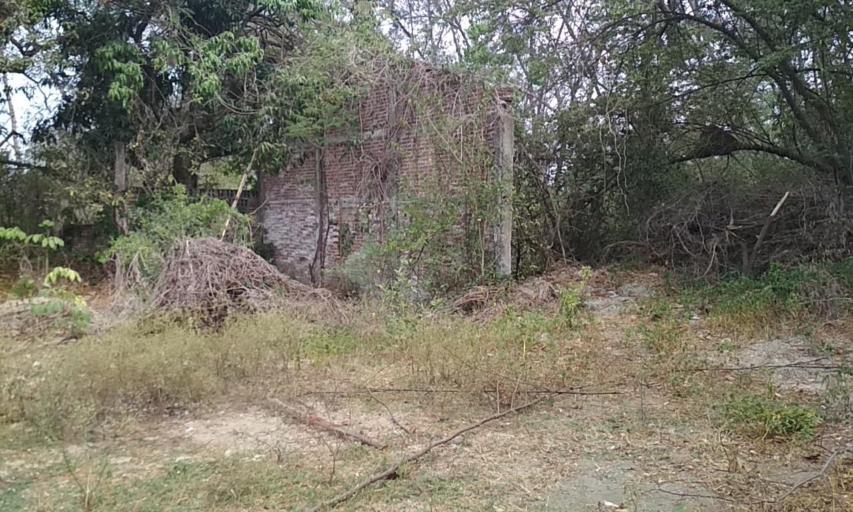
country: MX
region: Veracruz
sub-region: Veracruz
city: Las Amapolas
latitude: 19.1483
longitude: -96.2250
